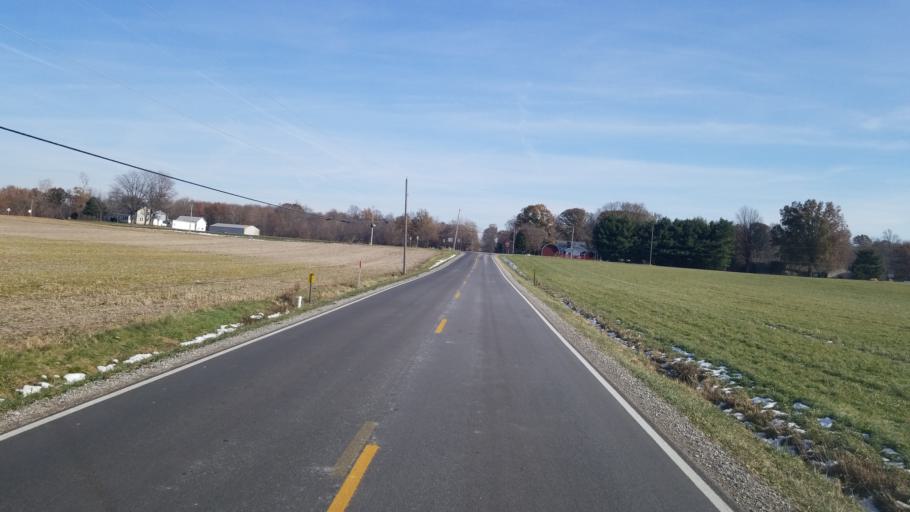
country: US
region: Ohio
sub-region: Huron County
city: Norwalk
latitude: 41.1917
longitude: -82.6288
